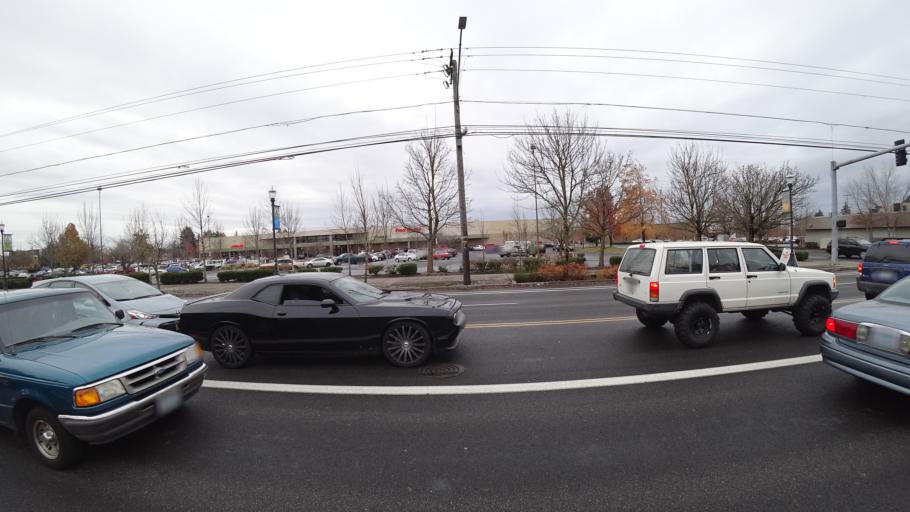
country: US
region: Oregon
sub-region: Multnomah County
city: Lents
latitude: 45.5309
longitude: -122.5580
